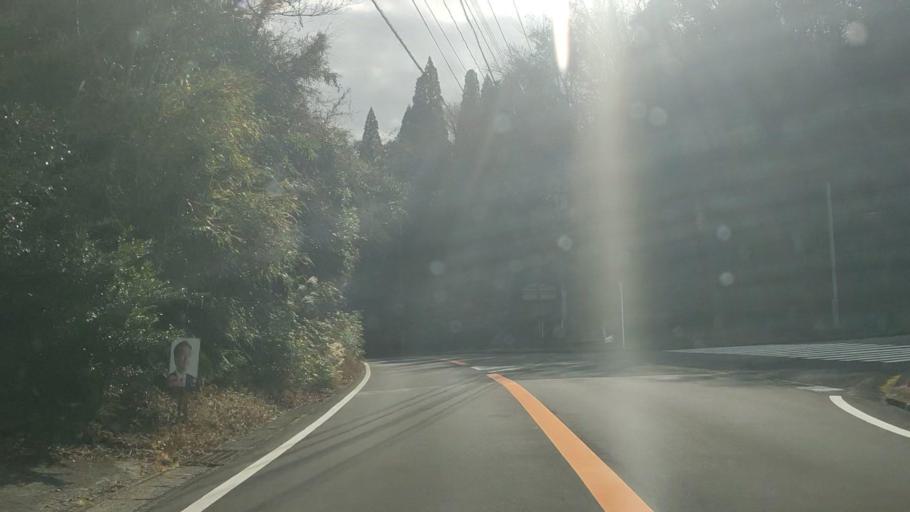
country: JP
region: Kagoshima
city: Kajiki
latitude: 31.8276
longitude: 130.6888
